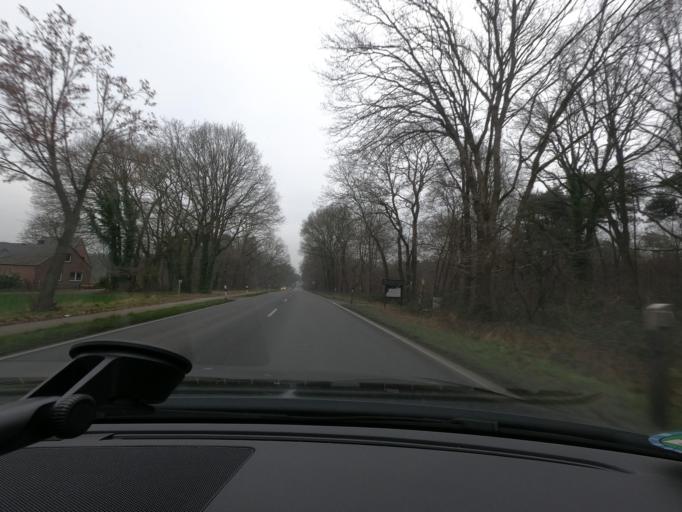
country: DE
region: North Rhine-Westphalia
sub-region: Regierungsbezirk Dusseldorf
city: Nettetal
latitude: 51.3498
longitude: 6.2345
